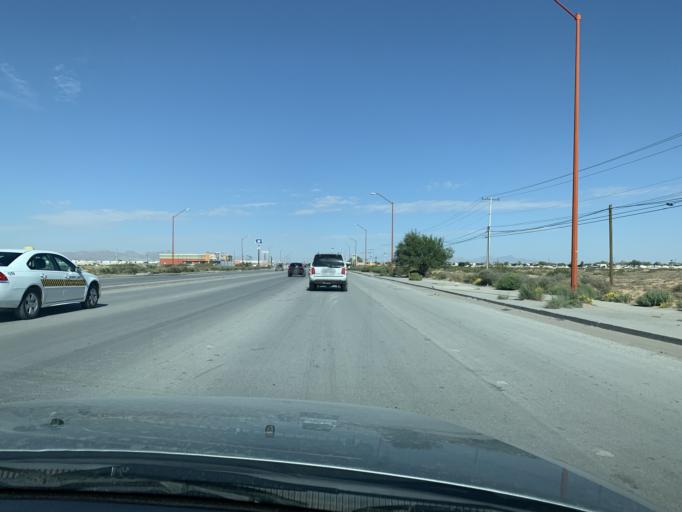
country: US
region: Texas
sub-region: El Paso County
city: San Elizario
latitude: 31.5766
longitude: -106.3556
